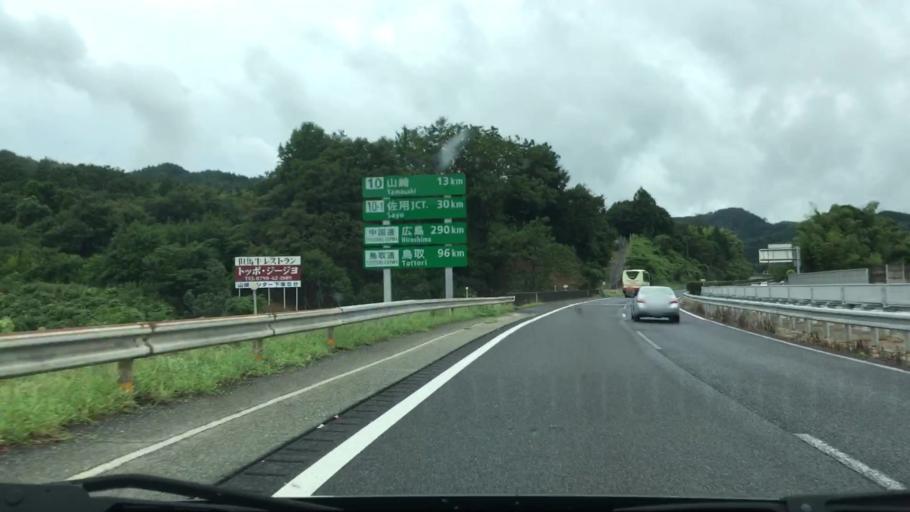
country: JP
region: Hyogo
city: Yamazakicho-nakabirose
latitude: 34.9640
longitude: 134.6800
